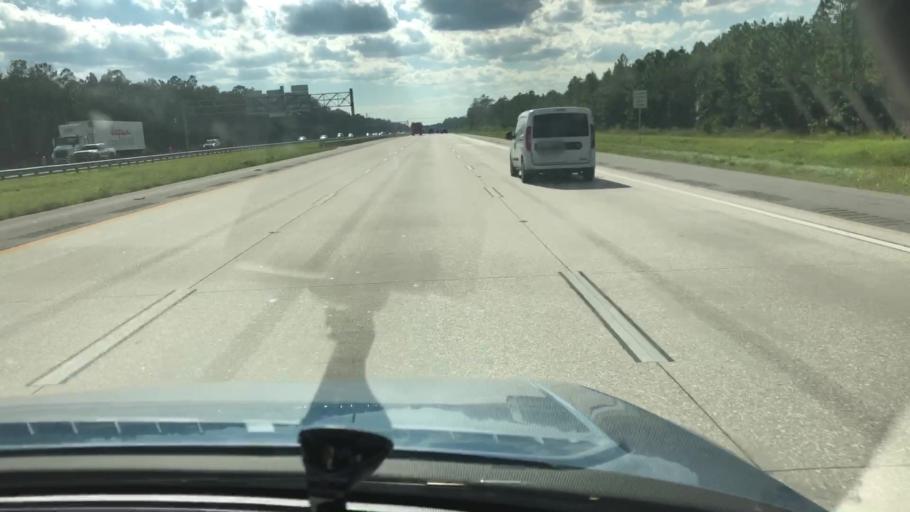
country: US
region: Florida
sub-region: Volusia County
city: South Daytona
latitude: 29.1477
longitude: -81.0954
